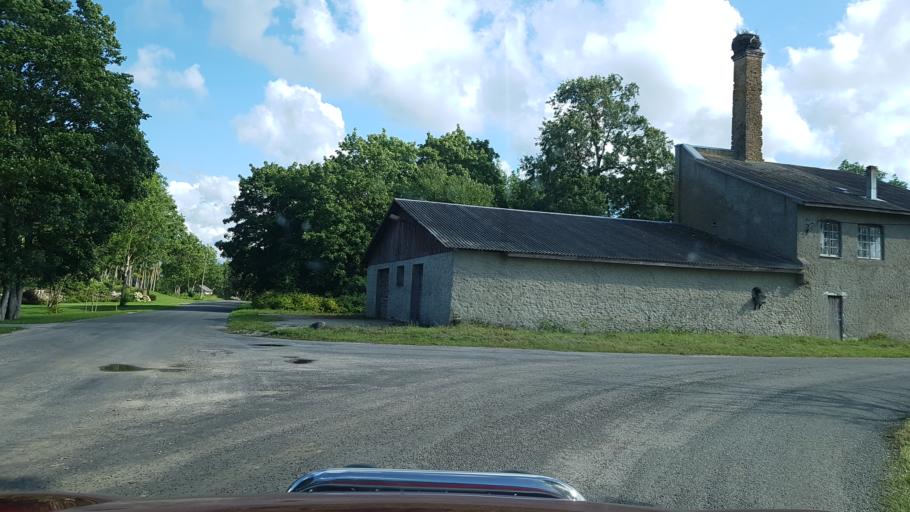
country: EE
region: Harju
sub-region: Paldiski linn
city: Paldiski
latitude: 59.2364
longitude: 24.0198
